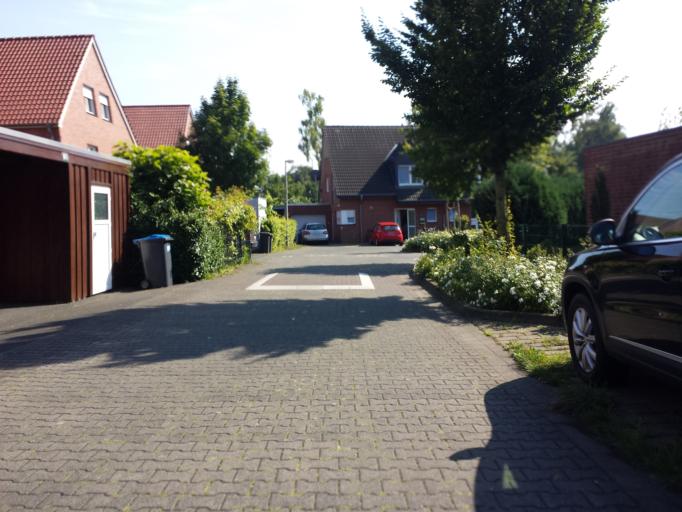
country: DE
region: North Rhine-Westphalia
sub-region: Regierungsbezirk Detmold
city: Guetersloh
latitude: 51.8802
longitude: 8.3770
